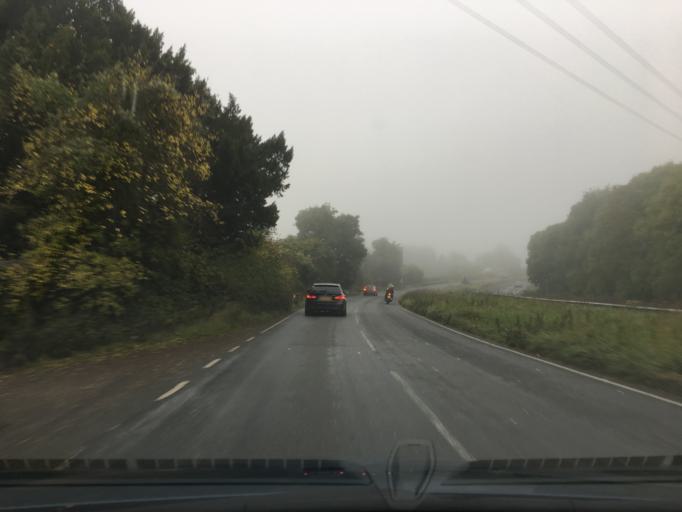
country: GB
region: England
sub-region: Hampshire
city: Four Marks
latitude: 51.1018
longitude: -1.0675
